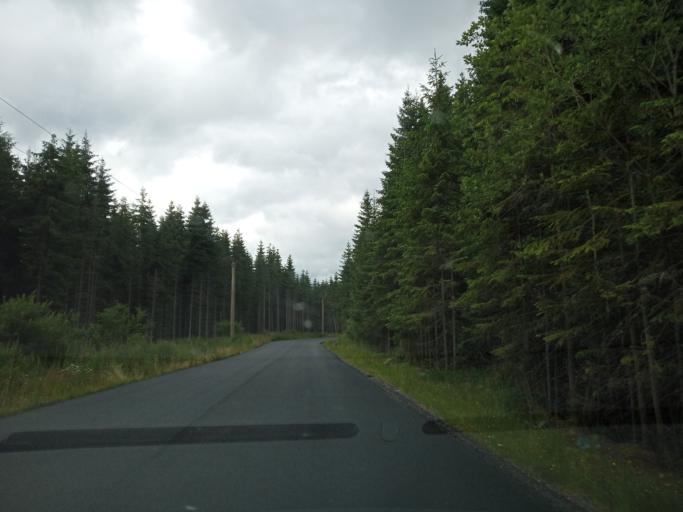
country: RO
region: Gorj
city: Novaci-Straini
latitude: 45.4239
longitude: 23.6923
